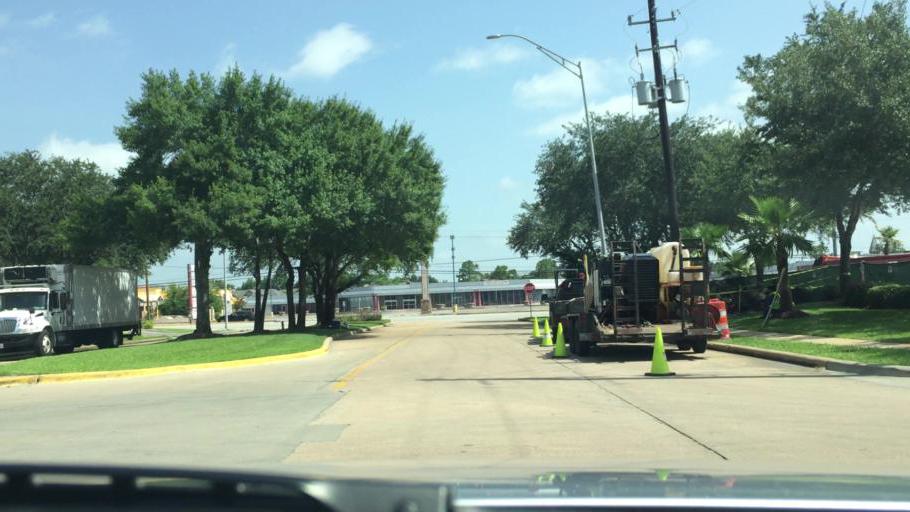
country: US
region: Texas
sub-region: Harris County
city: Bunker Hill Village
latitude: 29.7354
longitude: -95.5956
